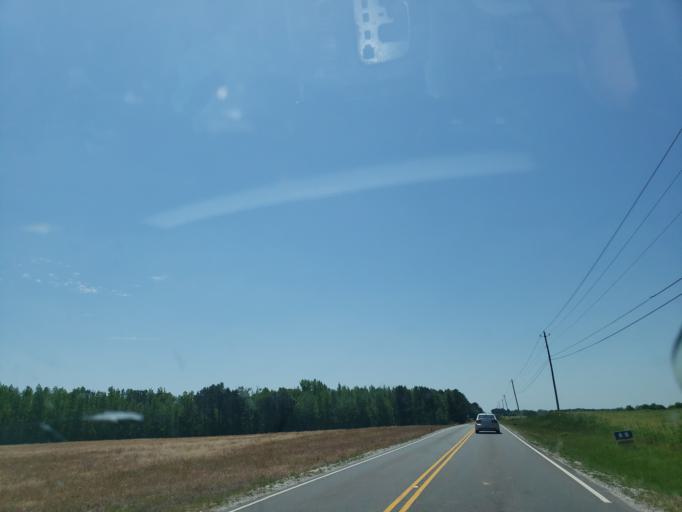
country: US
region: Alabama
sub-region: Madison County
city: Harvest
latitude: 34.8747
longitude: -86.7431
